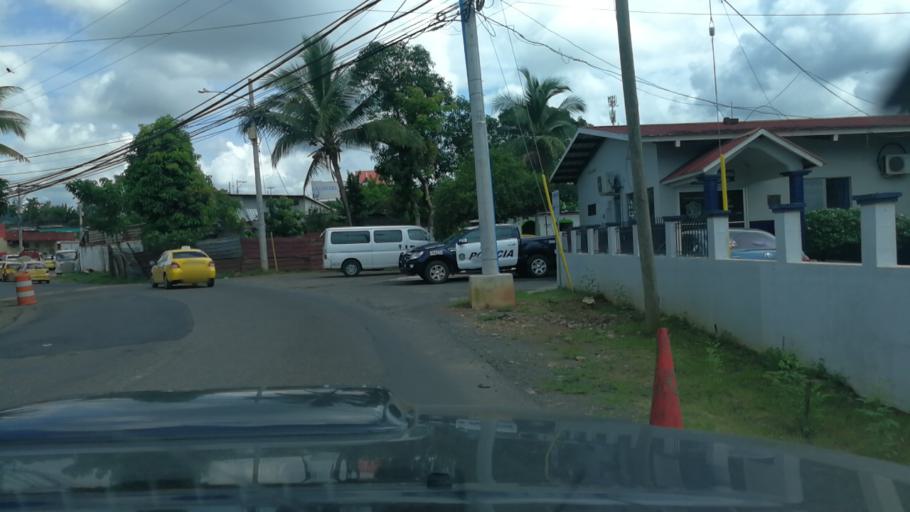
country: PA
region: Panama
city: Tocumen
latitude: 9.0965
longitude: -79.4089
